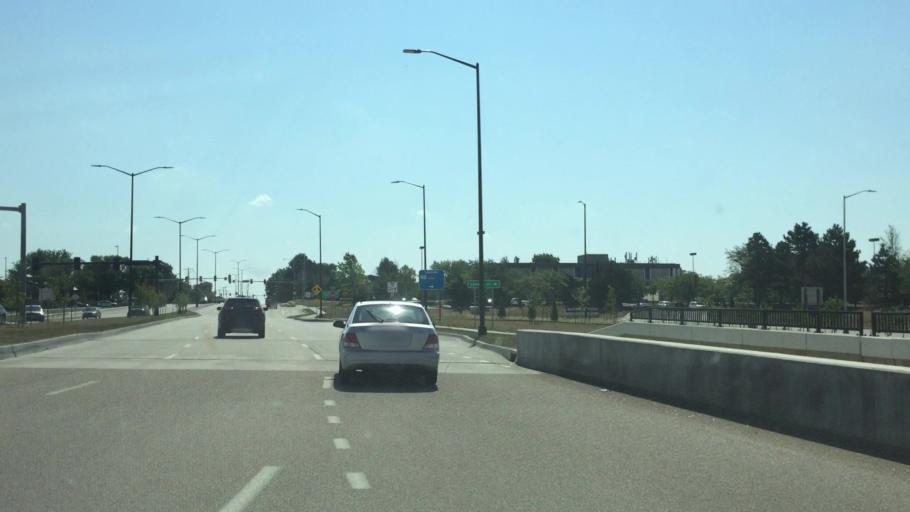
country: US
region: Kansas
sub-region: Johnson County
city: Lenexa
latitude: 38.9564
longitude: -94.7312
